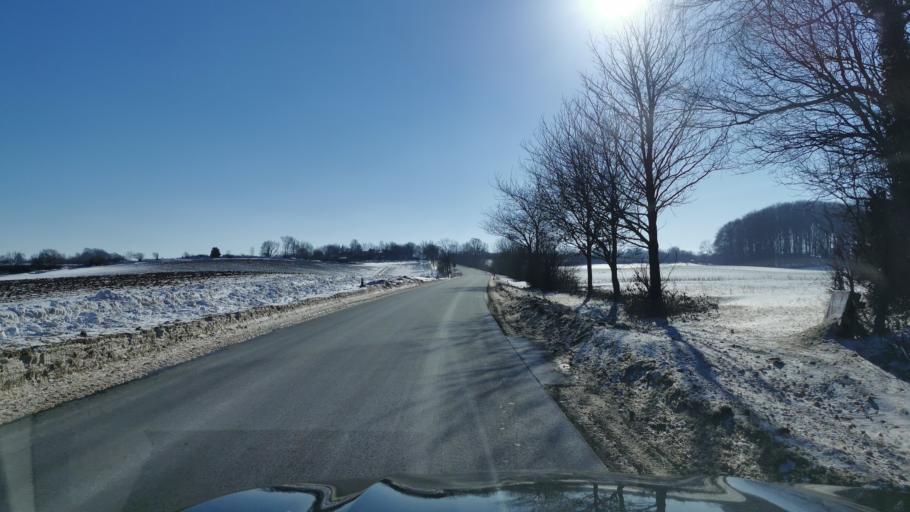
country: DE
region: Schleswig-Holstein
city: Grundhof
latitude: 54.7866
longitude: 9.6442
